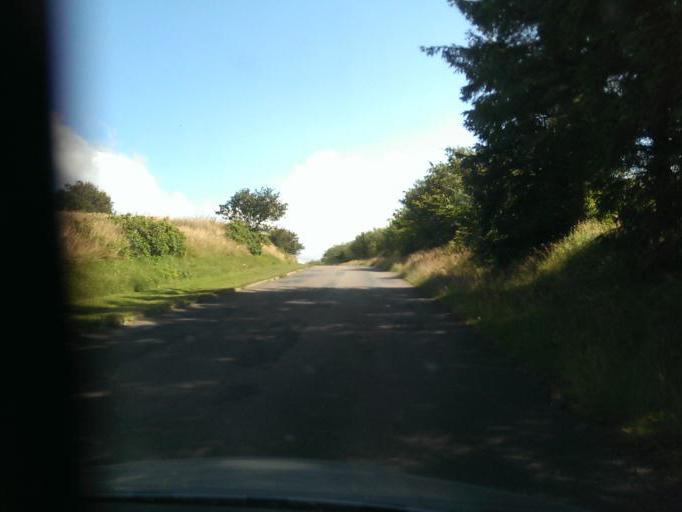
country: DK
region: North Denmark
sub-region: Jammerbugt Kommune
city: Pandrup
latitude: 57.3102
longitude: 9.7055
